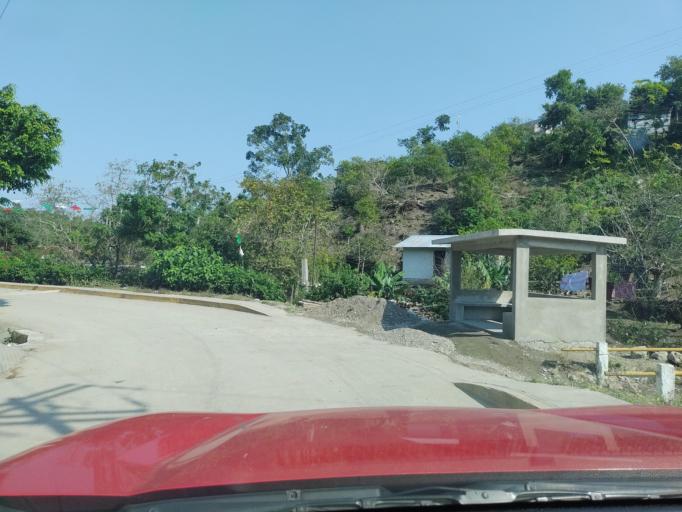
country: MX
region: Veracruz
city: Agua Dulce
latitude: 20.3490
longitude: -97.1760
